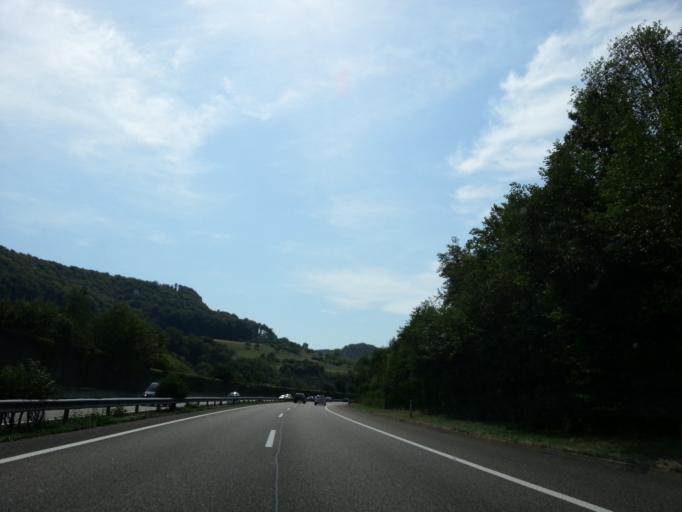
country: CH
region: Basel-Landschaft
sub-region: Bezirk Sissach
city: Zunzgen
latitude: 47.4478
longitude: 7.8050
